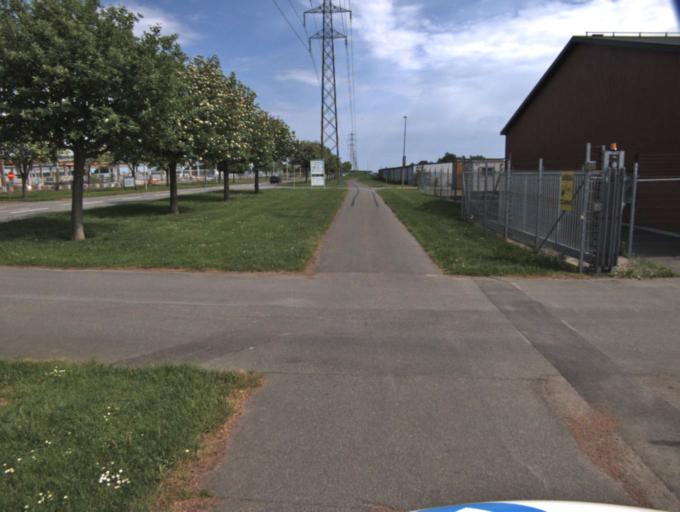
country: SE
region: Skane
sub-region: Kristianstads Kommun
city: Kristianstad
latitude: 56.0574
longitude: 14.1705
